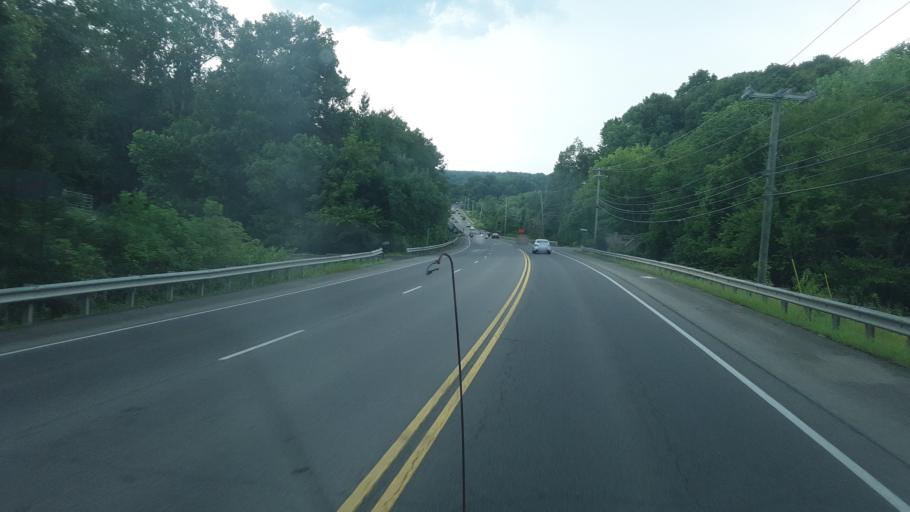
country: US
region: Tennessee
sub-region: Montgomery County
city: Clarksville
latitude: 36.5245
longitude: -87.2782
